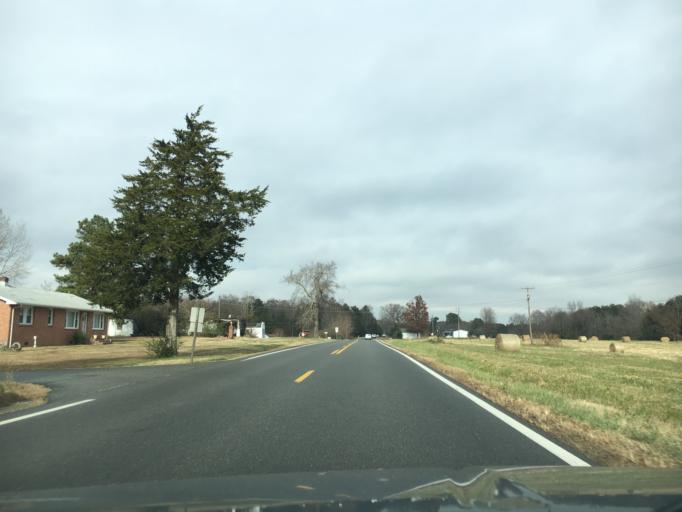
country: US
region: Virginia
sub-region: Prince Edward County
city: Farmville
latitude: 37.3563
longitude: -78.3798
